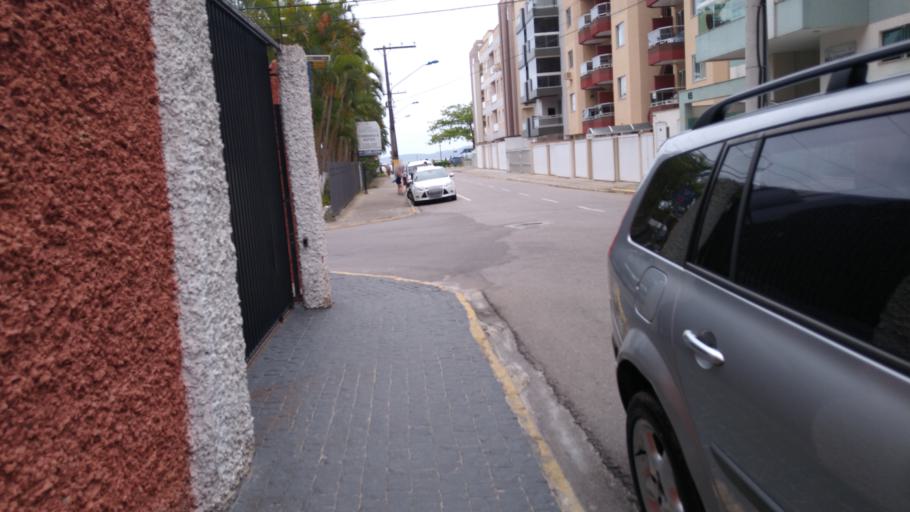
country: BR
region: Santa Catarina
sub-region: Itapema
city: Itapema
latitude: -27.0968
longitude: -48.6146
